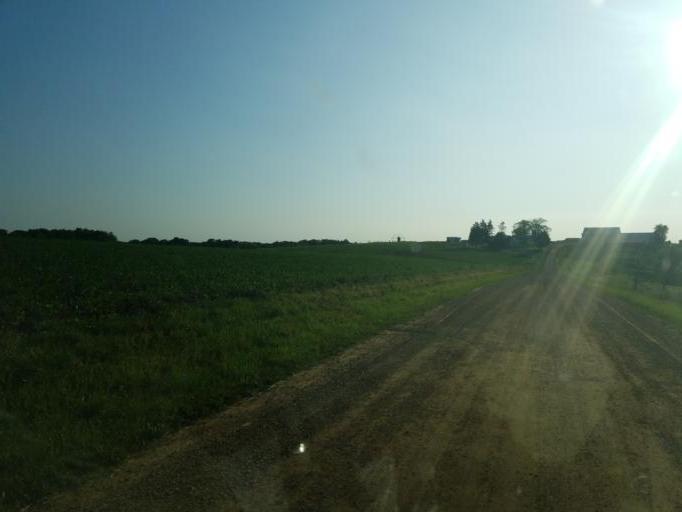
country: US
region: Wisconsin
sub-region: Vernon County
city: Hillsboro
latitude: 43.6227
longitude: -90.3241
